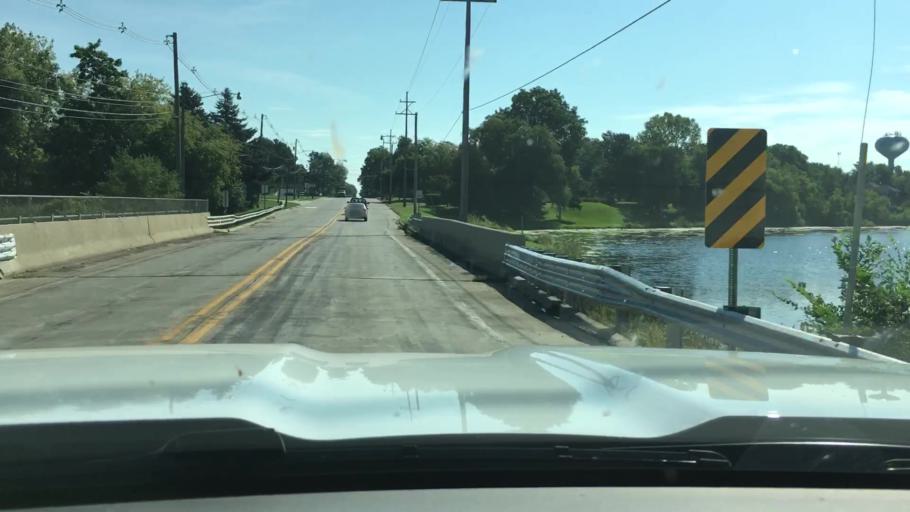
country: US
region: Michigan
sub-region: Gratiot County
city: Saint Louis
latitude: 43.4079
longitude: -84.6192
